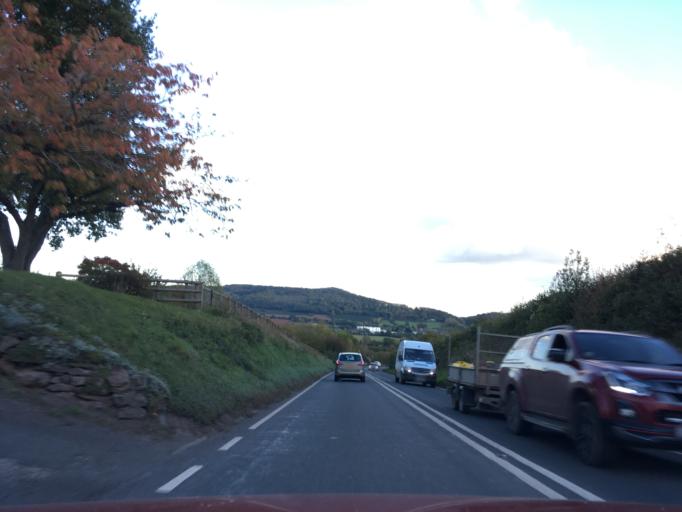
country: GB
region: England
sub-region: Herefordshire
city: Ledbury
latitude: 52.0509
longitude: -2.4533
